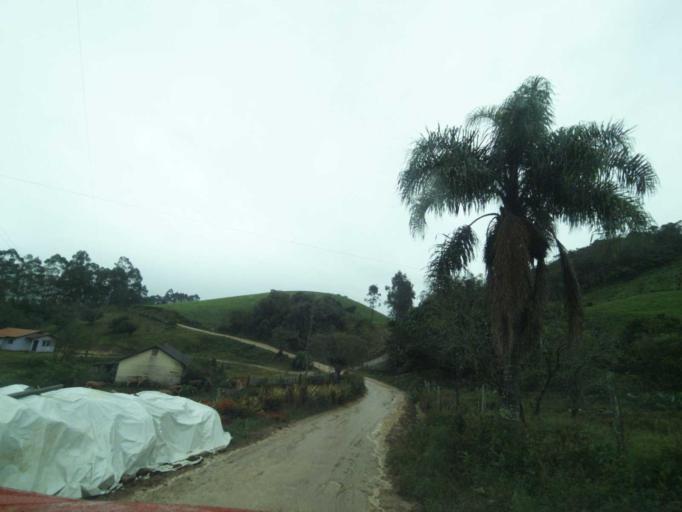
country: BR
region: Santa Catarina
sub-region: Anitapolis
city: Anitapolis
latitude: -27.8882
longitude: -49.1965
